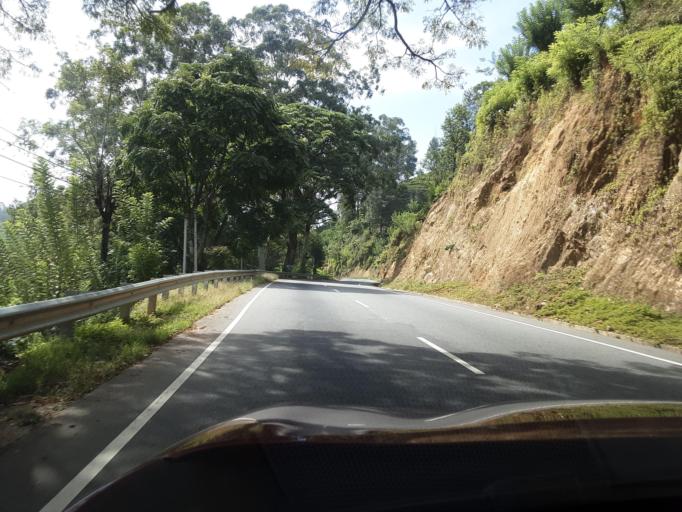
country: LK
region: Uva
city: Badulla
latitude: 6.9604
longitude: 81.1133
